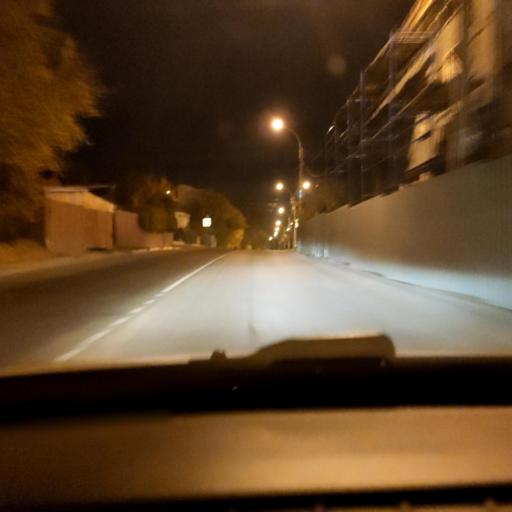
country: RU
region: Voronezj
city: Voronezh
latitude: 51.6568
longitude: 39.2131
